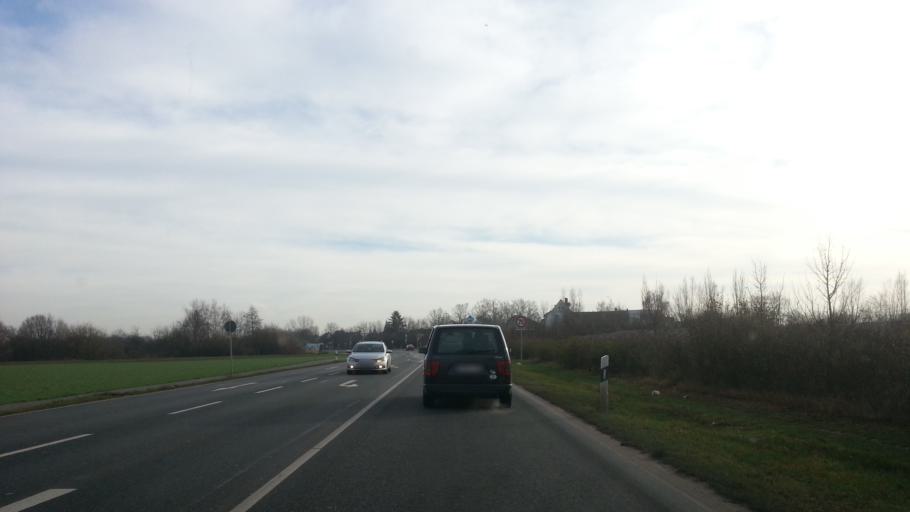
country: DE
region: Hesse
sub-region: Regierungsbezirk Darmstadt
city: Buttelborn
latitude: 49.9084
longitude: 8.5012
